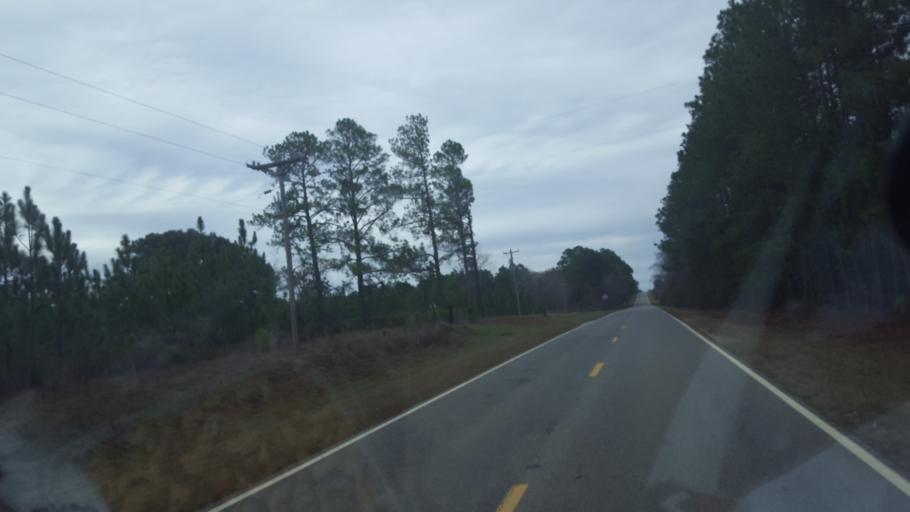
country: US
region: Georgia
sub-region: Ben Hill County
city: Fitzgerald
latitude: 31.7829
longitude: -83.4063
